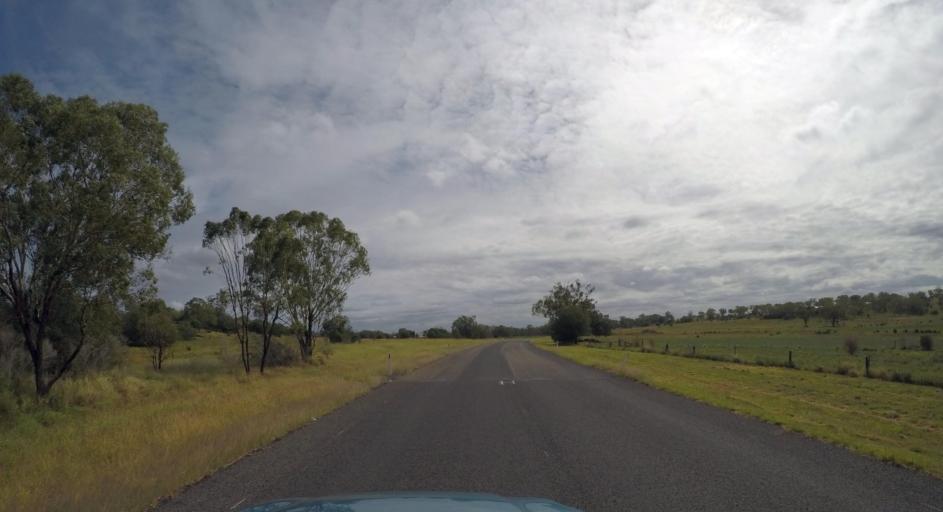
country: AU
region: Queensland
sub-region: Western Downs
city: Dalby
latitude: -27.0433
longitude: 151.3090
